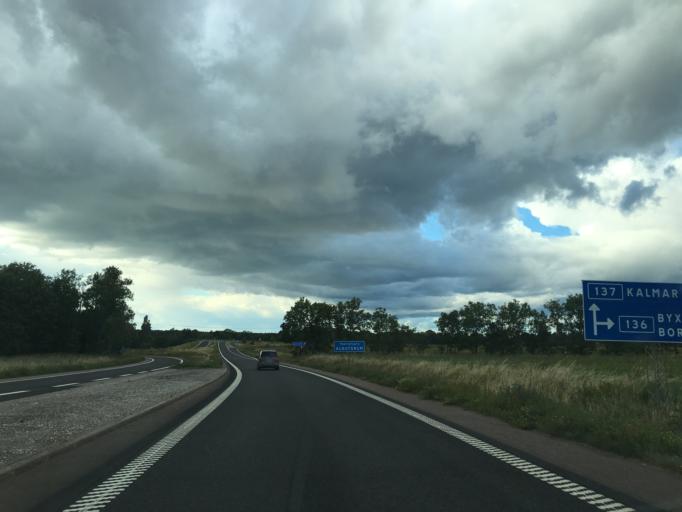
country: SE
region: Kalmar
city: Faerjestaden
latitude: 56.6683
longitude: 16.5181
